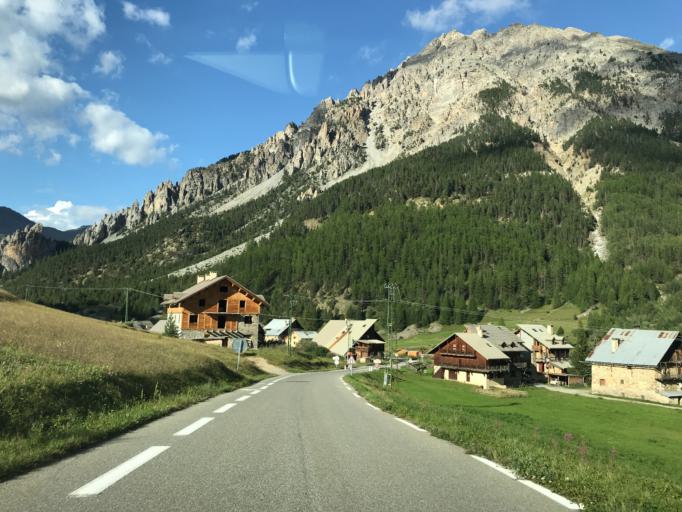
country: IT
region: Piedmont
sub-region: Provincia di Torino
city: Claviere
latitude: 44.8533
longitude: 6.7252
